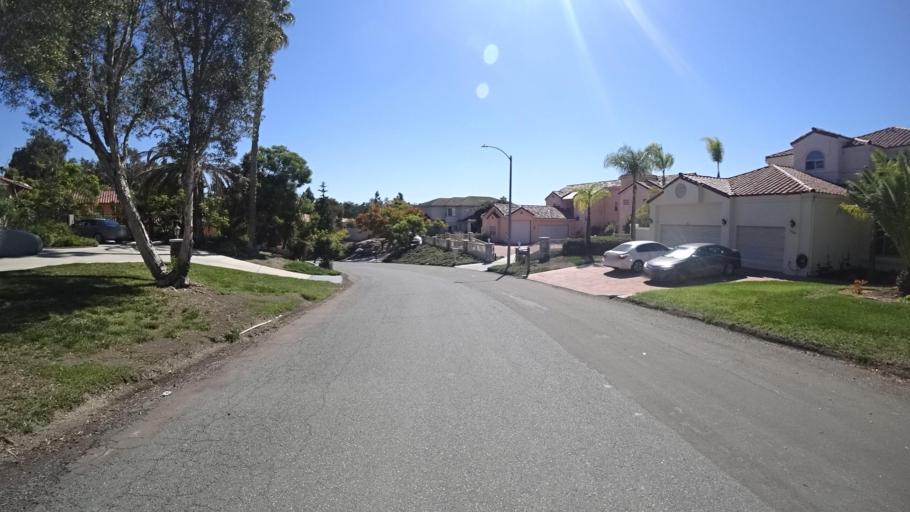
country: US
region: California
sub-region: San Diego County
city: Bonita
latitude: 32.6602
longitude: -117.0133
